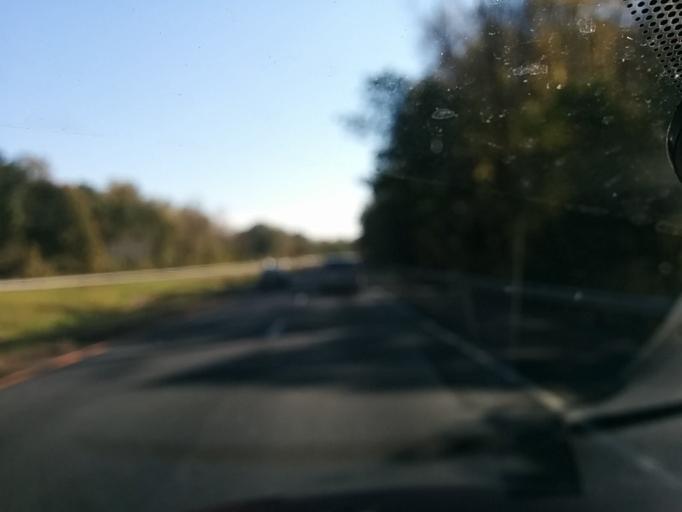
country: US
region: Virginia
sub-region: City of Charlottesville
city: Charlottesville
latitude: 38.0223
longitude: -78.5482
